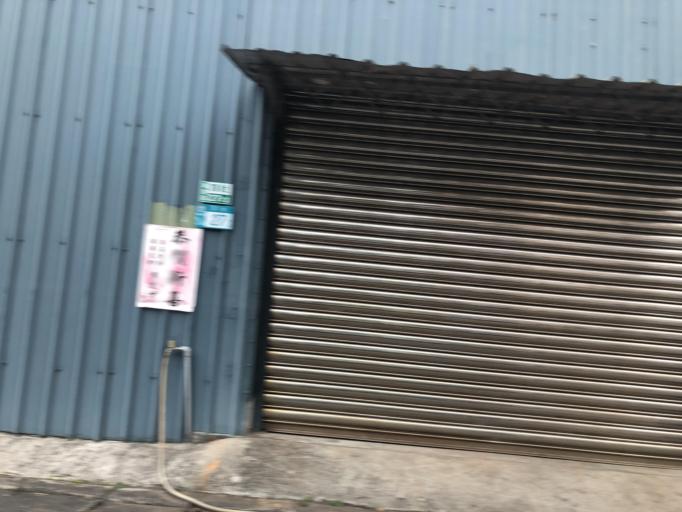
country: TW
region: Taiwan
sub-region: Keelung
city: Keelung
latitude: 25.2106
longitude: 121.6570
